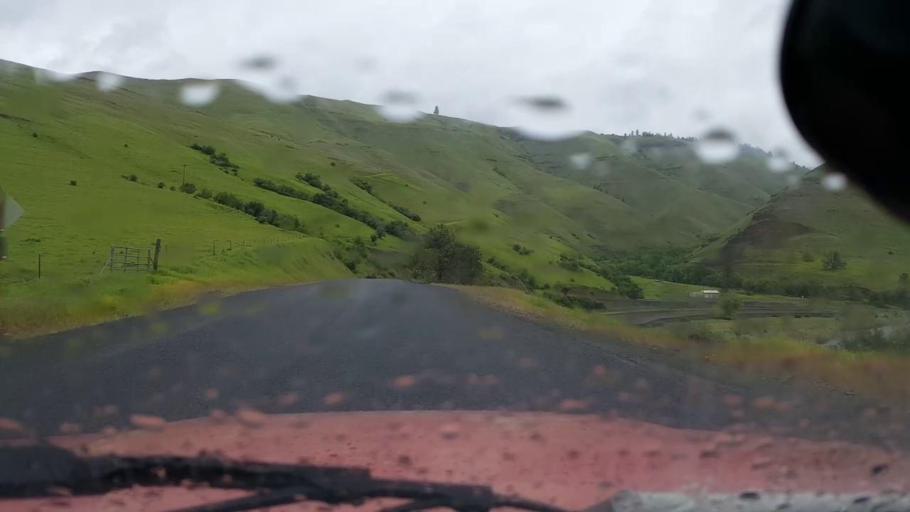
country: US
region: Washington
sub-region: Asotin County
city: Asotin
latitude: 46.0339
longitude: -117.2947
